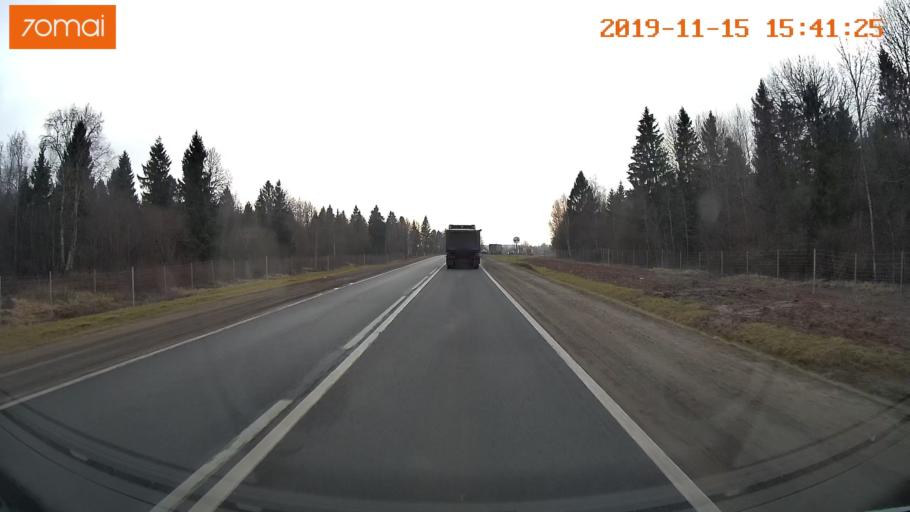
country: RU
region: Jaroslavl
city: Danilov
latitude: 58.0008
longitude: 40.0482
